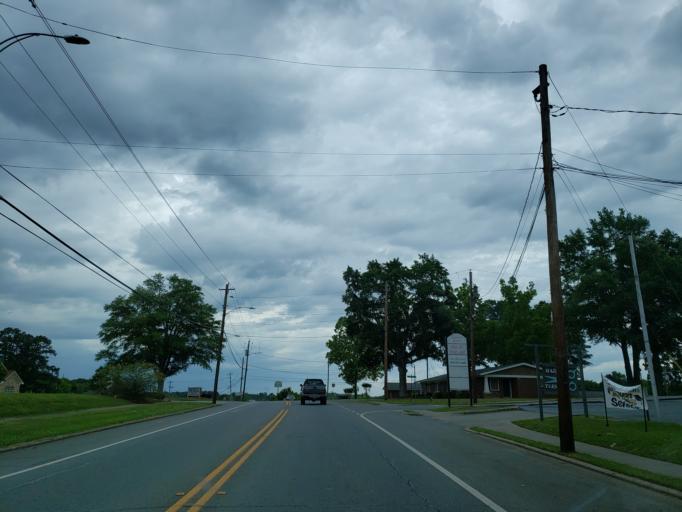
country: US
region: Georgia
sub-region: Polk County
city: Rockmart
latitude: 34.0051
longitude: -85.0414
